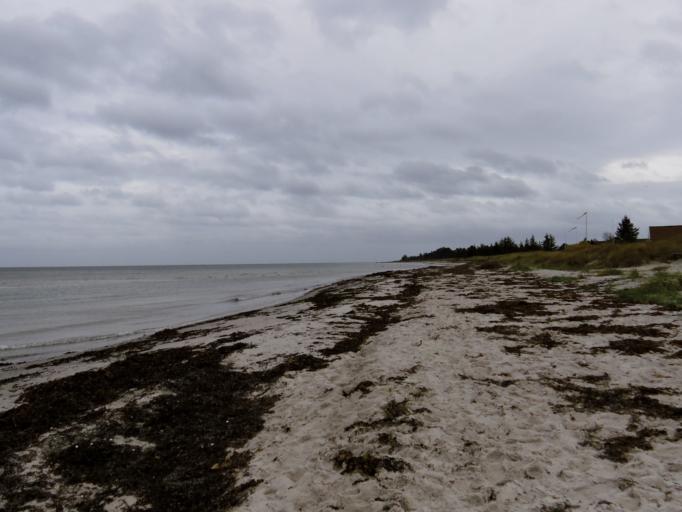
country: DK
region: Central Jutland
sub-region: Arhus Kommune
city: Malling
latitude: 55.9762
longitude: 10.2539
